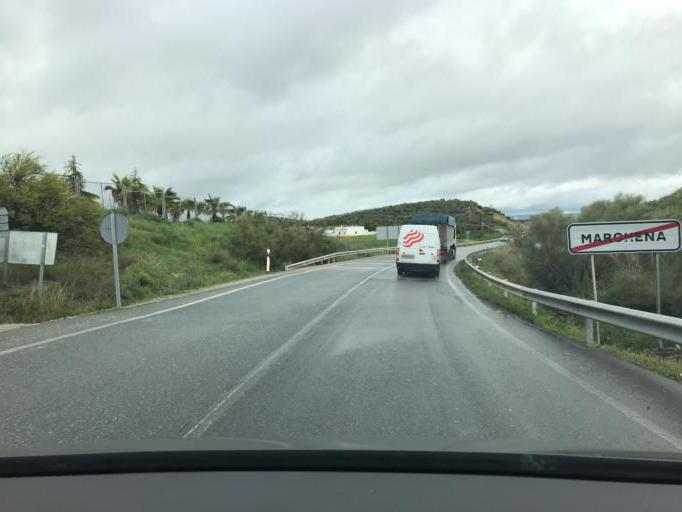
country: ES
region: Andalusia
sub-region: Provincia de Sevilla
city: Marchena
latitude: 37.3303
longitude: -5.4084
